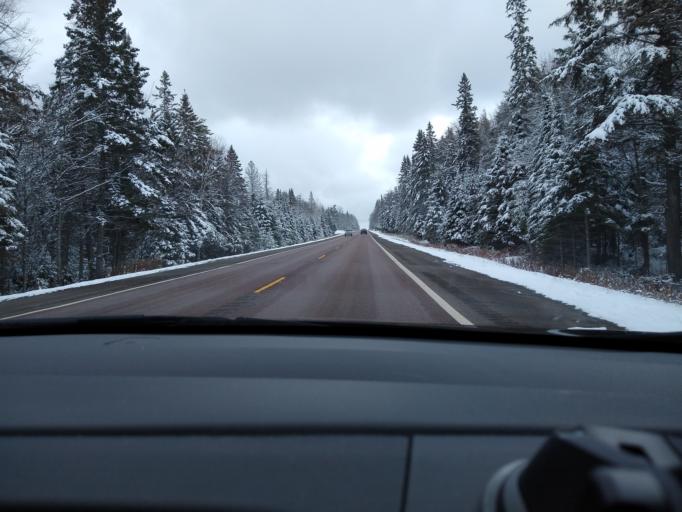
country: US
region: Wisconsin
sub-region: Vilas County
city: Eagle River
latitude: 46.2246
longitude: -89.0644
